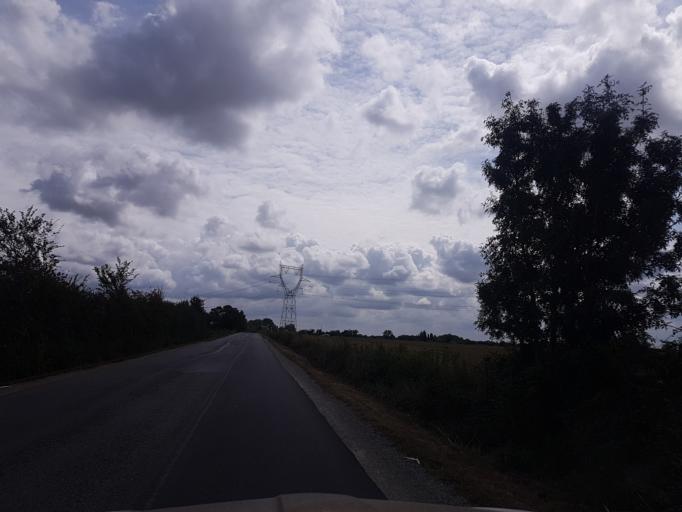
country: FR
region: Pays de la Loire
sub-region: Departement de la Loire-Atlantique
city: Les Touches
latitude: 47.4248
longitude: -1.4388
